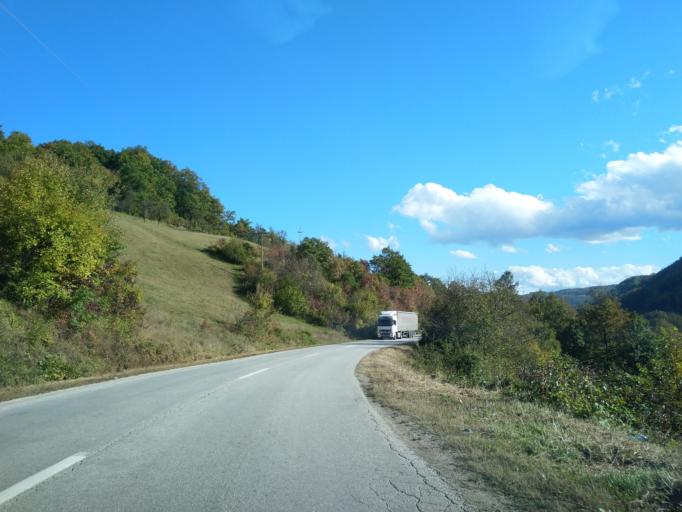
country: RS
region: Central Serbia
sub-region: Zlatiborski Okrug
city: Uzice
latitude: 43.8693
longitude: 19.8005
